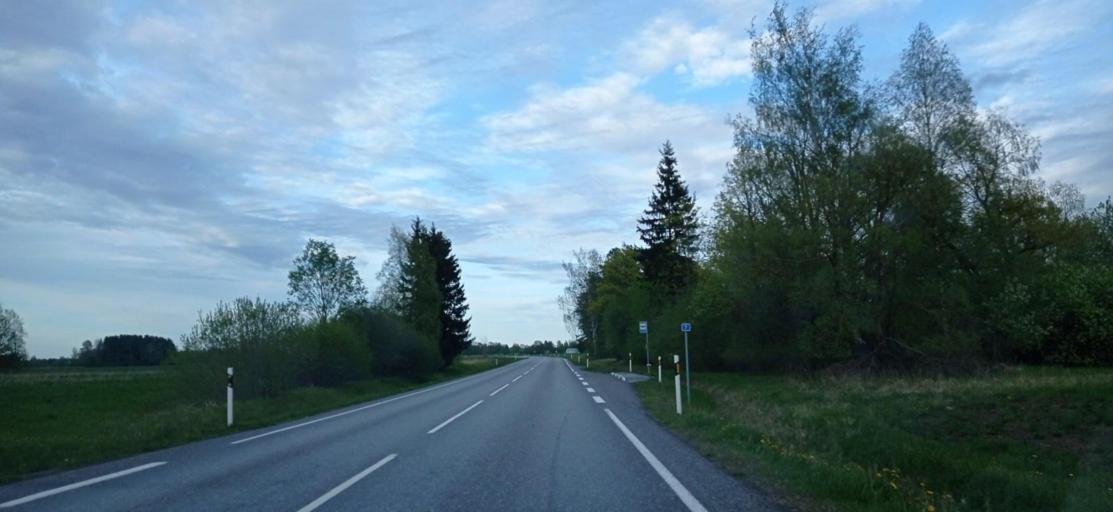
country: EE
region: Paernumaa
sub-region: Sindi linn
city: Sindi
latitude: 58.5273
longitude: 24.6722
